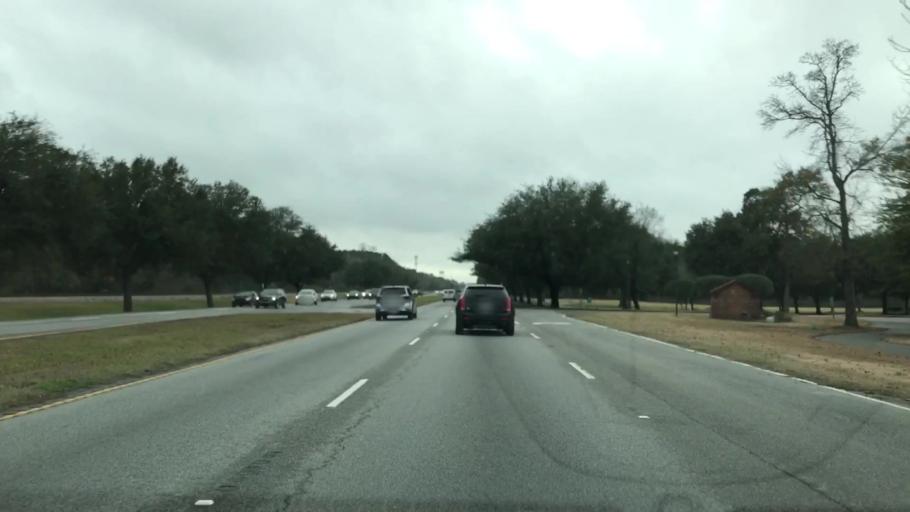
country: US
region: South Carolina
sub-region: Berkeley County
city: Goose Creek
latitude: 33.0284
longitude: -80.0350
